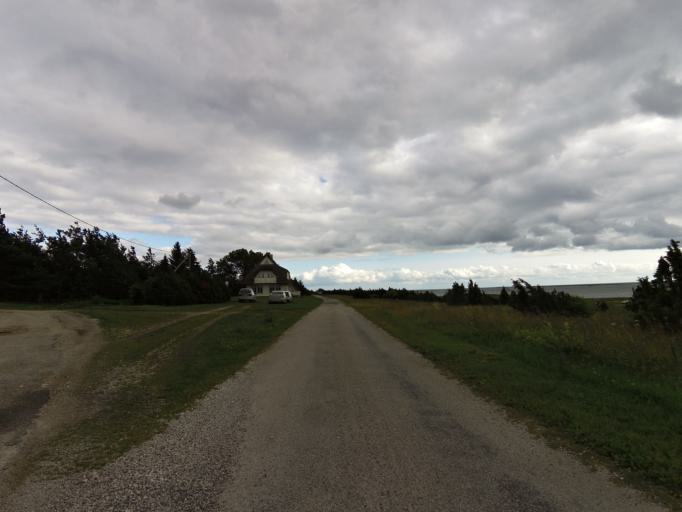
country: EE
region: Laeaene
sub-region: Vormsi vald
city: Hullo
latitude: 58.9718
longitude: 23.2638
